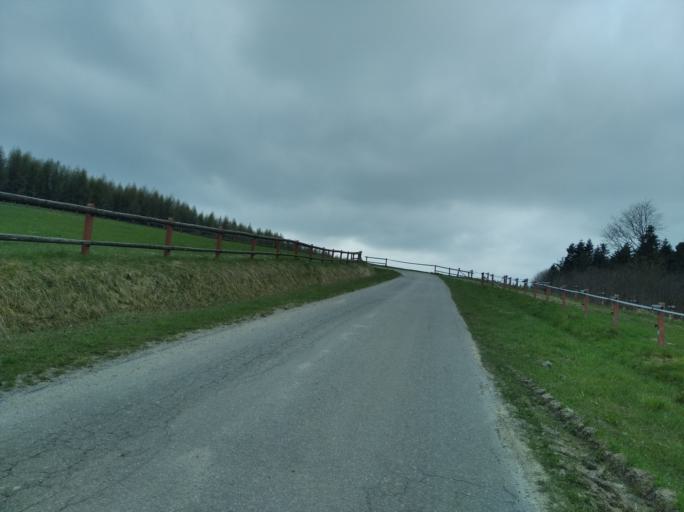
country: PL
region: Subcarpathian Voivodeship
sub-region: Powiat strzyzowski
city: Konieczkowa
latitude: 49.8234
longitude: 21.9129
